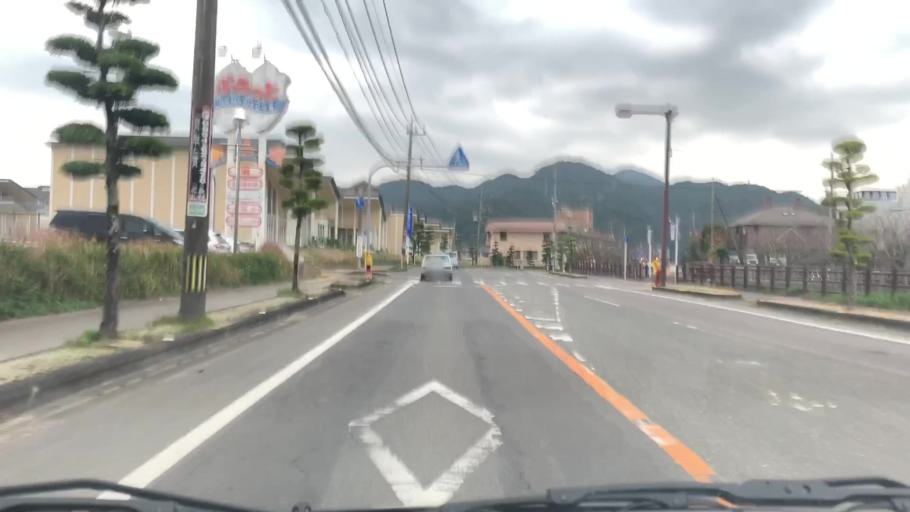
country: JP
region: Saga Prefecture
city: Kashima
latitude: 33.1300
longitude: 130.0610
